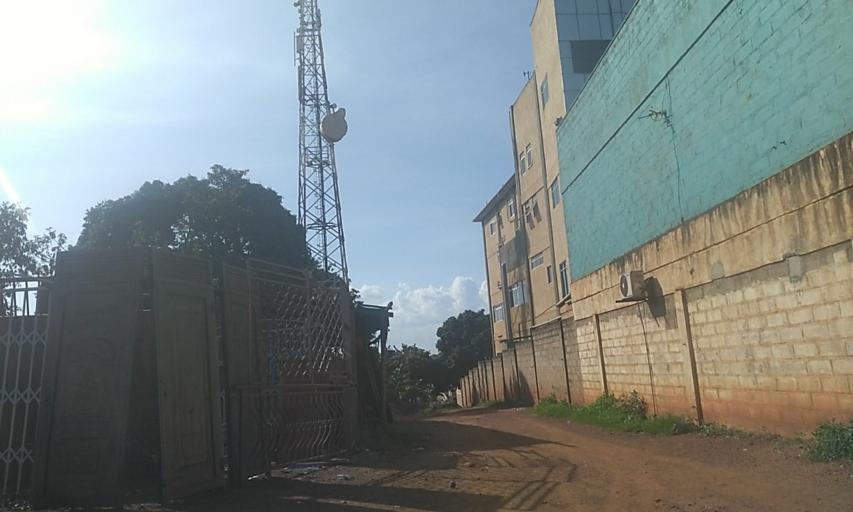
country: UG
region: Central Region
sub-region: Wakiso District
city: Kireka
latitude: 0.3634
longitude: 32.6259
